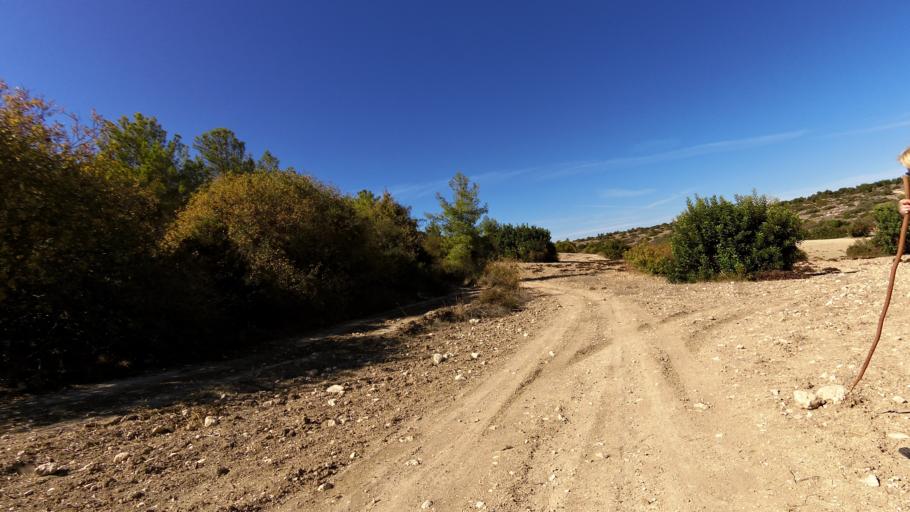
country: CY
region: Pafos
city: Polis
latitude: 35.0152
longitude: 32.4842
